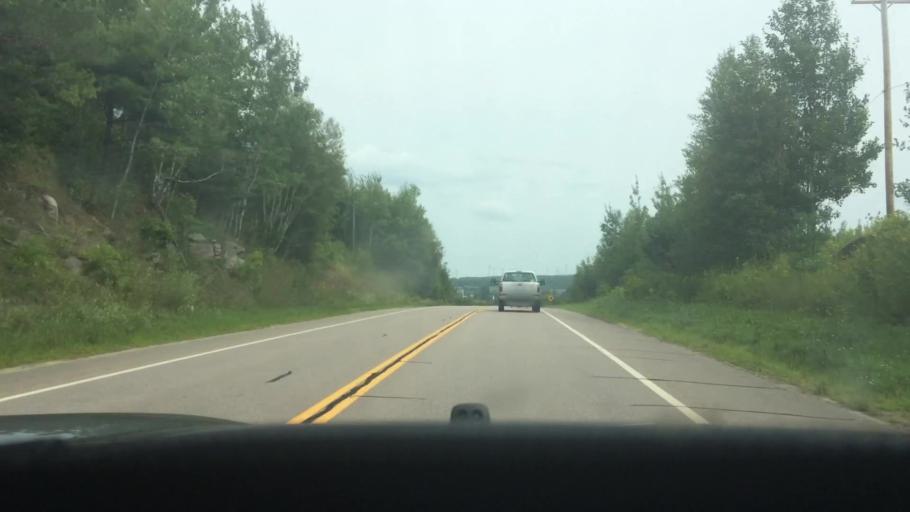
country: US
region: New York
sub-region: Franklin County
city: Malone
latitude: 44.8565
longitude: -74.0523
